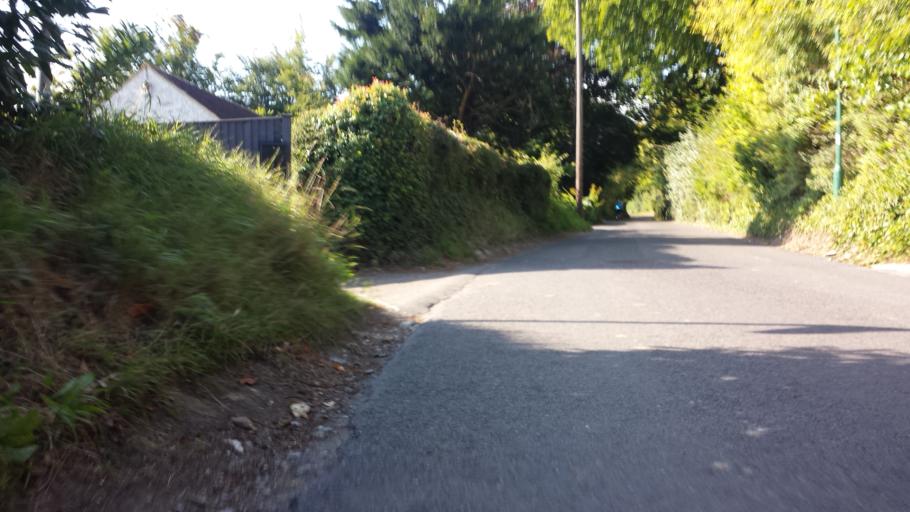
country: GB
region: England
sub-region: Kent
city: Eynsford
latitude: 51.3707
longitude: 0.2073
